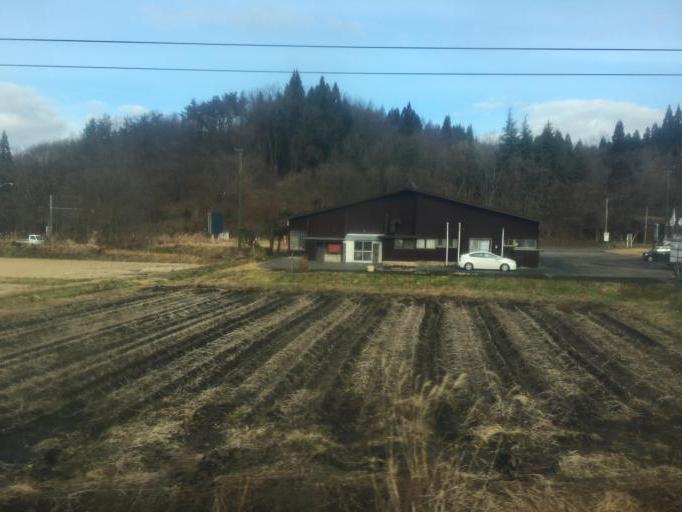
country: JP
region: Akita
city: Takanosu
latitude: 40.2630
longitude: 140.4304
